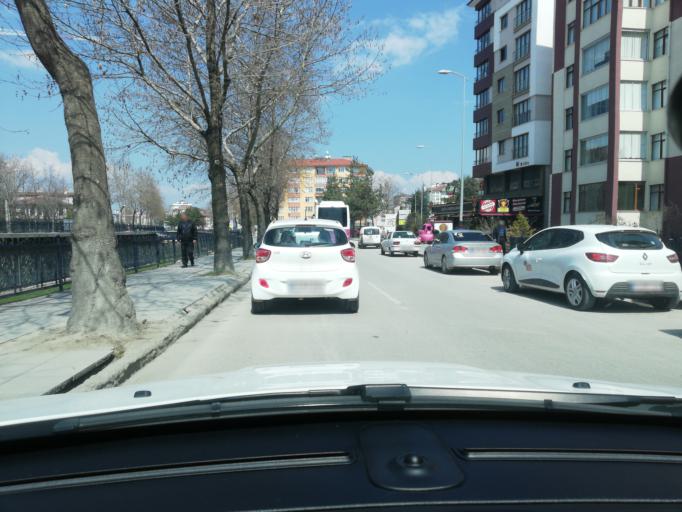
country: TR
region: Kastamonu
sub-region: Cide
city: Kastamonu
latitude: 41.3898
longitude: 33.7812
